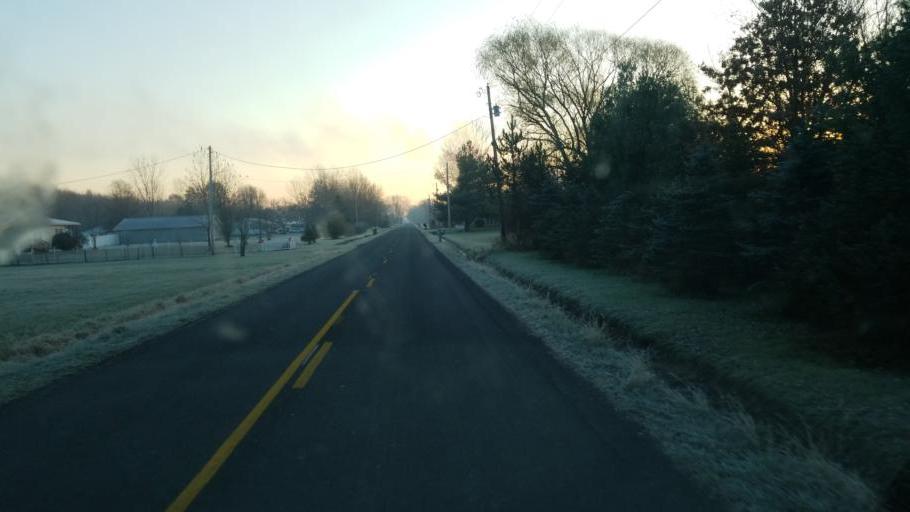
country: US
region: Ohio
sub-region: Medina County
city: Lodi
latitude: 41.0006
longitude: -82.0350
